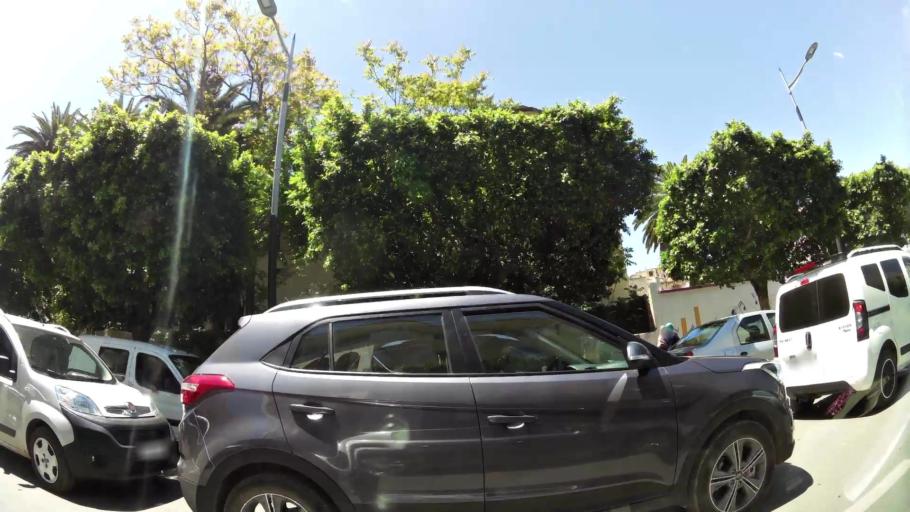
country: MA
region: Meknes-Tafilalet
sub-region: Meknes
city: Meknes
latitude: 33.8995
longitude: -5.5469
